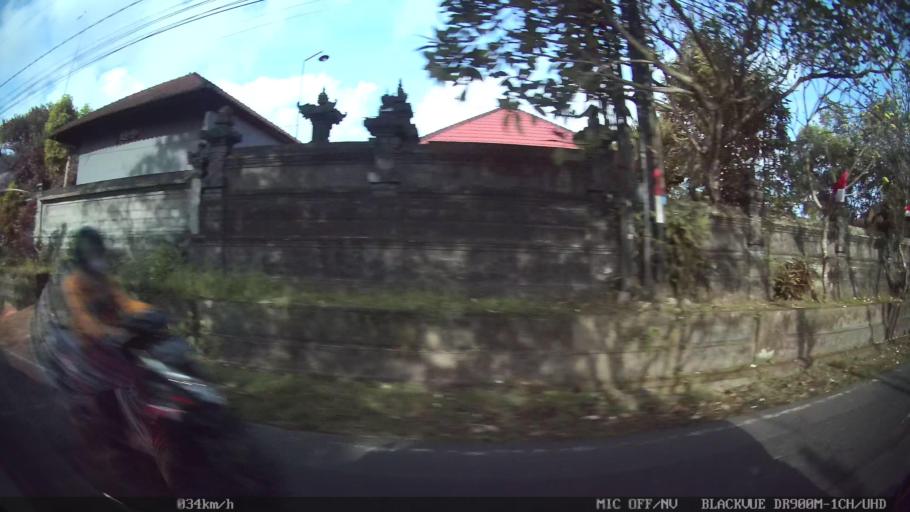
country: ID
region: Bali
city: Banjar Sedang
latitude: -8.5644
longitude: 115.2343
